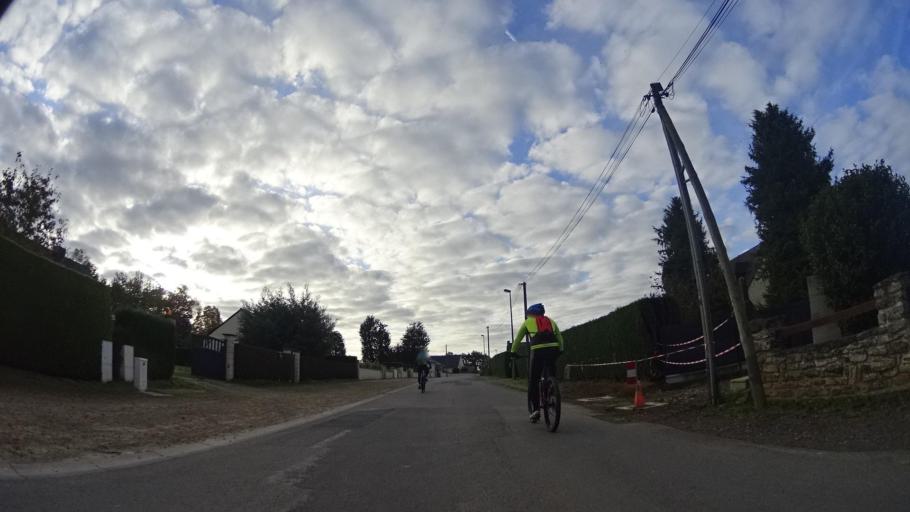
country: FR
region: Brittany
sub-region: Departement des Cotes-d'Armor
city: Evran
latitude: 48.3789
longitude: -1.9690
